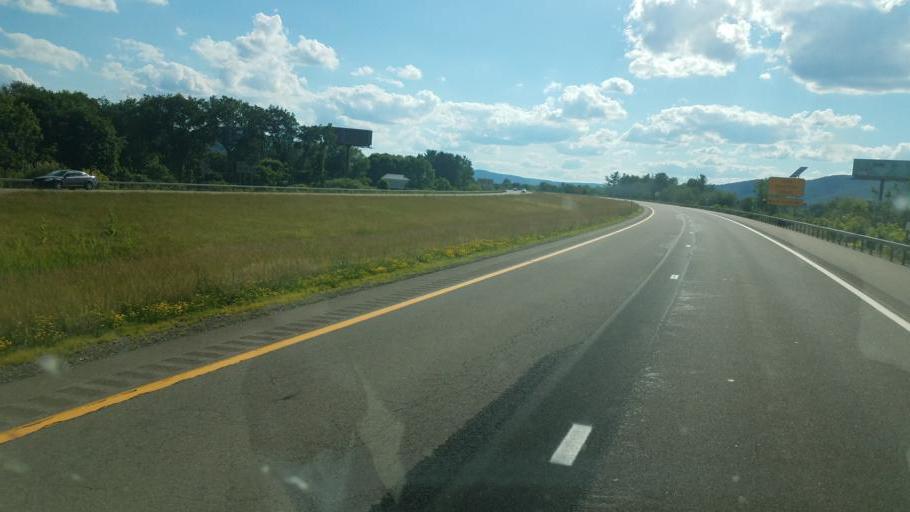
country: US
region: New York
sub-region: Cattaraugus County
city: Allegany
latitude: 42.1029
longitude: -78.5158
